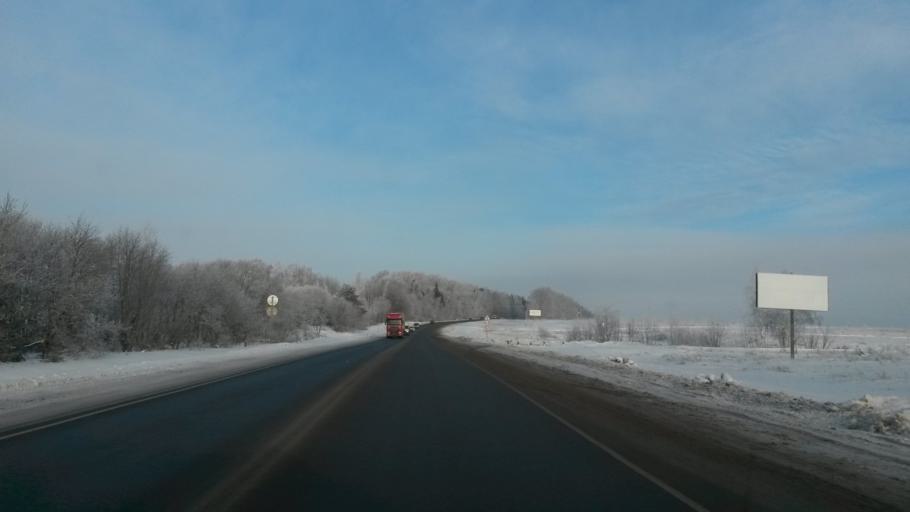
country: RU
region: Vladimir
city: Bogolyubovo
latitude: 56.2222
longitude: 40.4419
